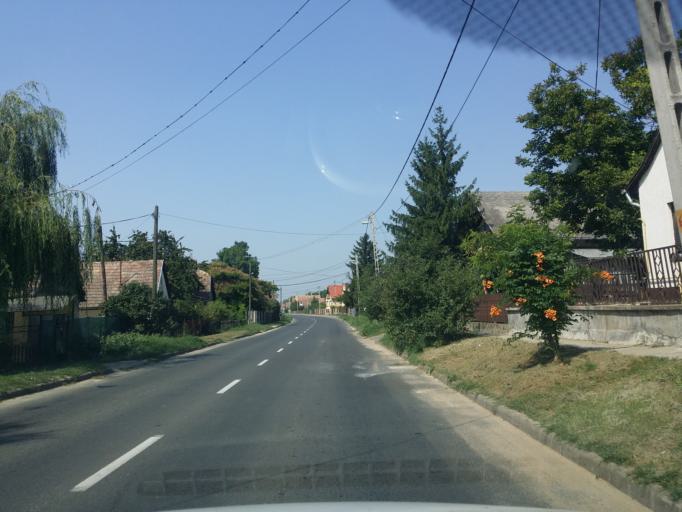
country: HU
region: Tolna
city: Pincehely
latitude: 46.7092
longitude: 18.4713
